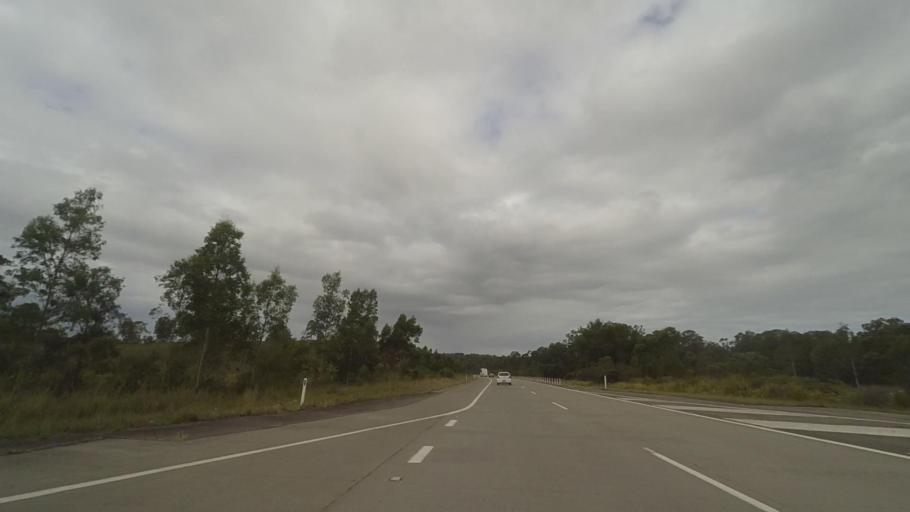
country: AU
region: New South Wales
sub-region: Port Stephens Shire
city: Port Stephens
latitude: -32.6374
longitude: 152.0343
